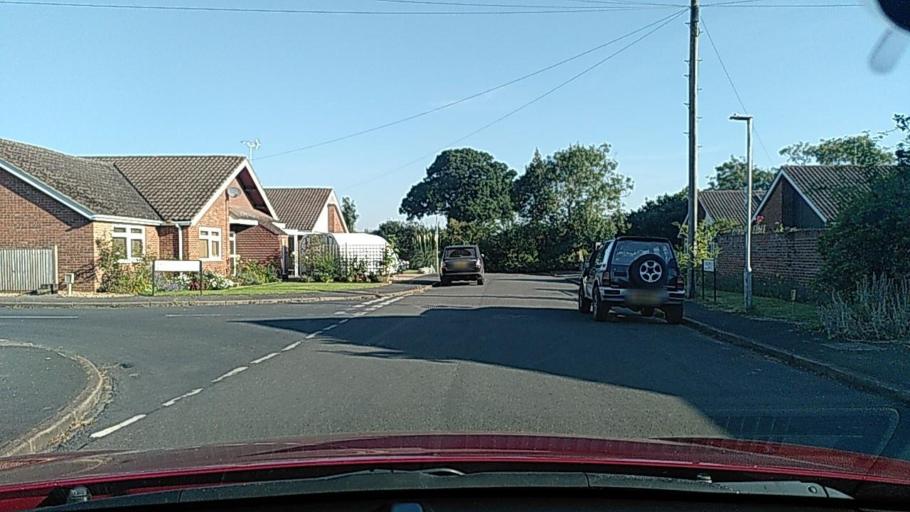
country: GB
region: England
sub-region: Oxfordshire
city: Sonning Common
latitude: 51.4926
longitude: -0.9581
